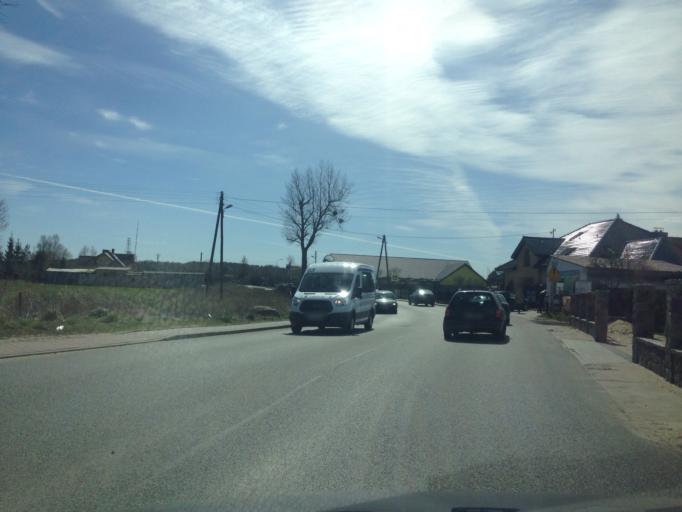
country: PL
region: Pomeranian Voivodeship
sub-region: Powiat kartuski
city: Chwaszczyno
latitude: 54.4841
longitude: 18.4377
